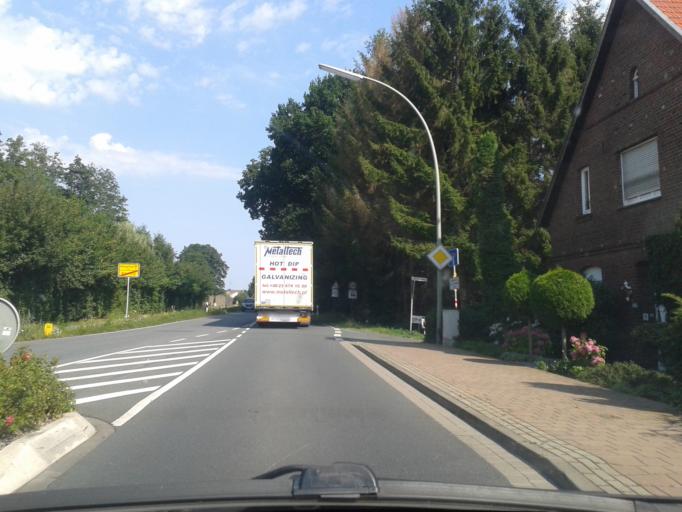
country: DE
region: North Rhine-Westphalia
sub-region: Regierungsbezirk Detmold
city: Verl
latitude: 51.8555
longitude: 8.5708
